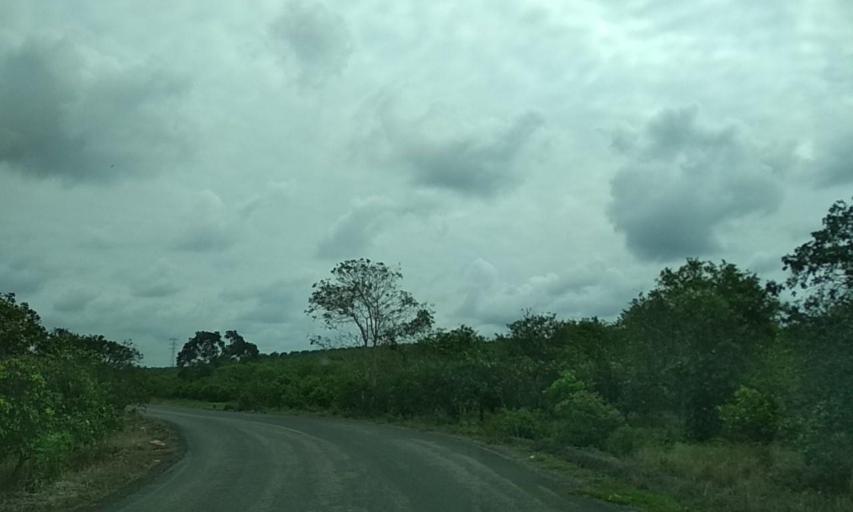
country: MX
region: Veracruz
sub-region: Papantla
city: El Chote
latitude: 20.3534
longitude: -97.3580
